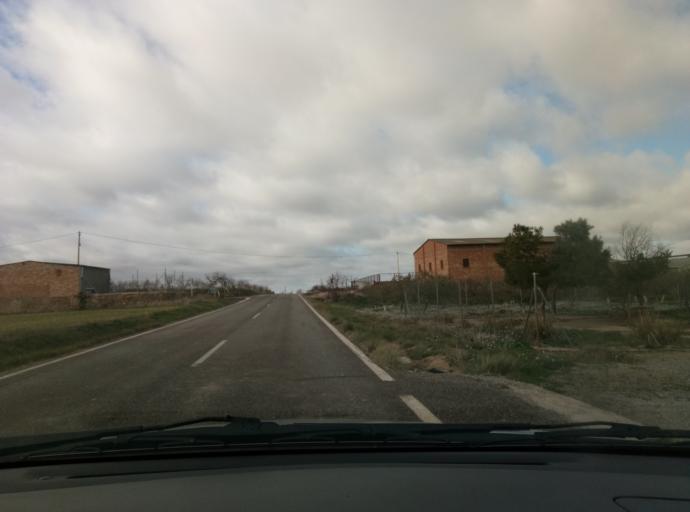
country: ES
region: Catalonia
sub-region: Provincia de Lleida
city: Vallbona de les Monges
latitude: 41.5618
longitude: 1.0653
